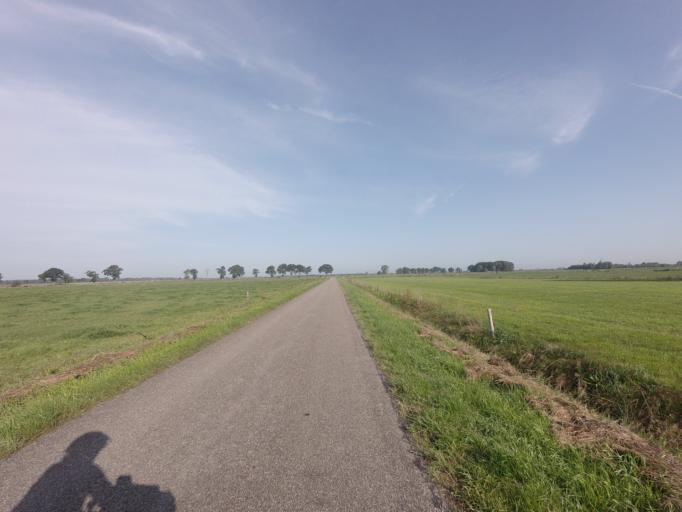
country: NL
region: Groningen
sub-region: Gemeente Leek
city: Leek
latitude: 53.1602
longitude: 6.4317
